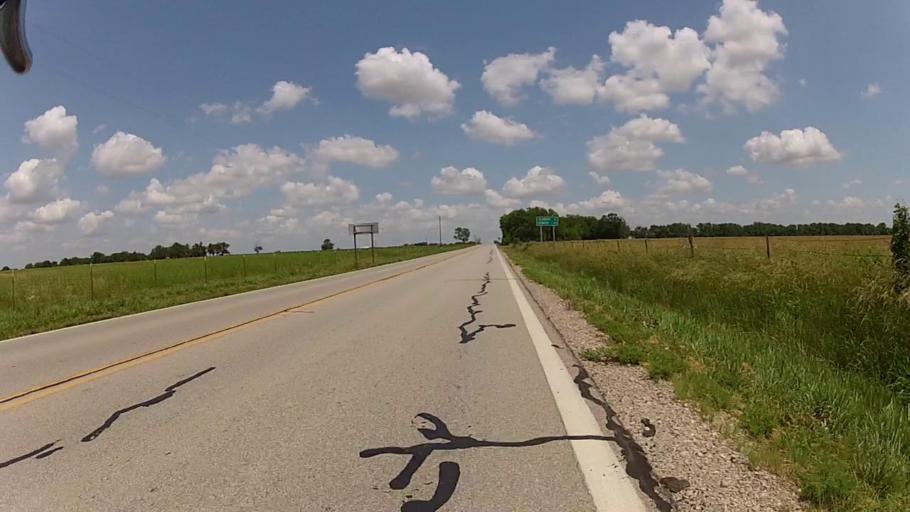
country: US
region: Kansas
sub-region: Labette County
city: Altamont
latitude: 37.1925
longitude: -95.3574
